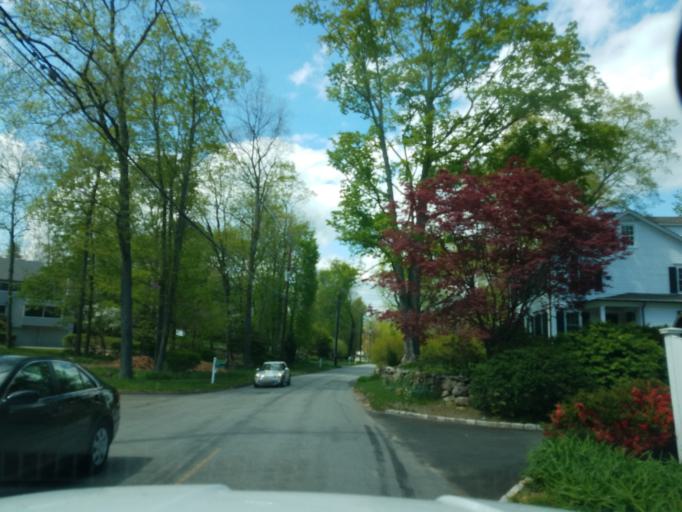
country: US
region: Connecticut
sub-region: Fairfield County
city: New Canaan
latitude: 41.1251
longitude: -73.4741
